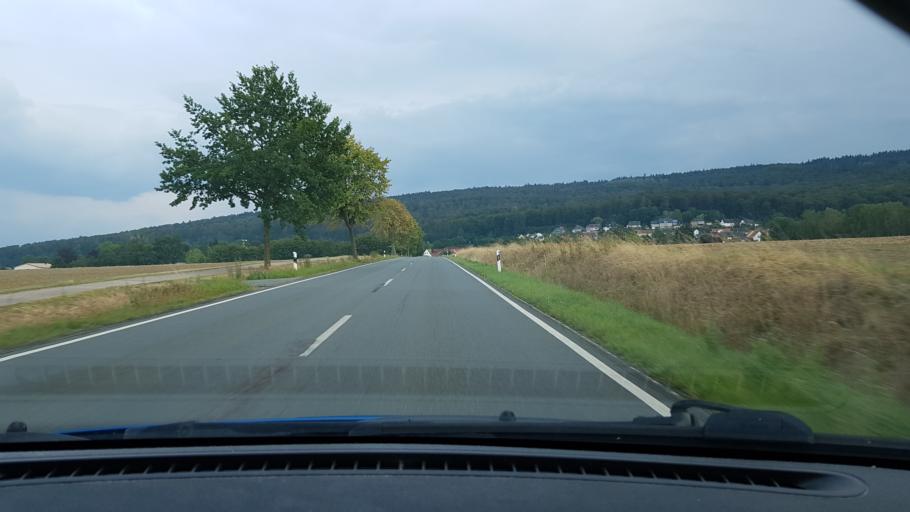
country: DE
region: Lower Saxony
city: Bad Munder am Deister
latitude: 52.1998
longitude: 9.4034
